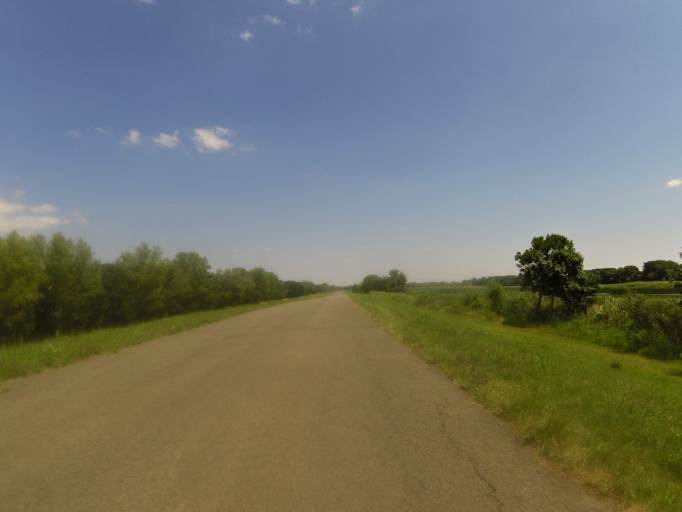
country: HU
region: Heves
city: Kiskore
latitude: 47.5094
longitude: 20.5459
